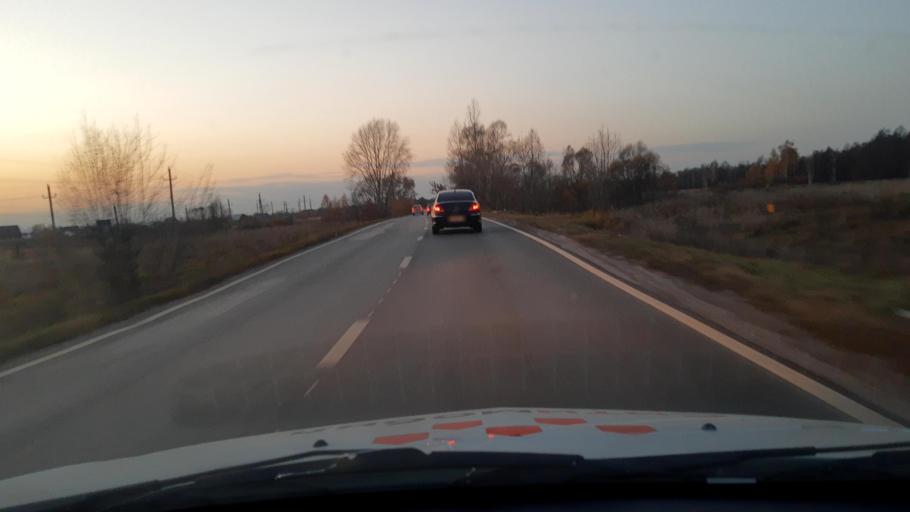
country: RU
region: Bashkortostan
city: Iglino
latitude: 54.7434
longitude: 56.2184
